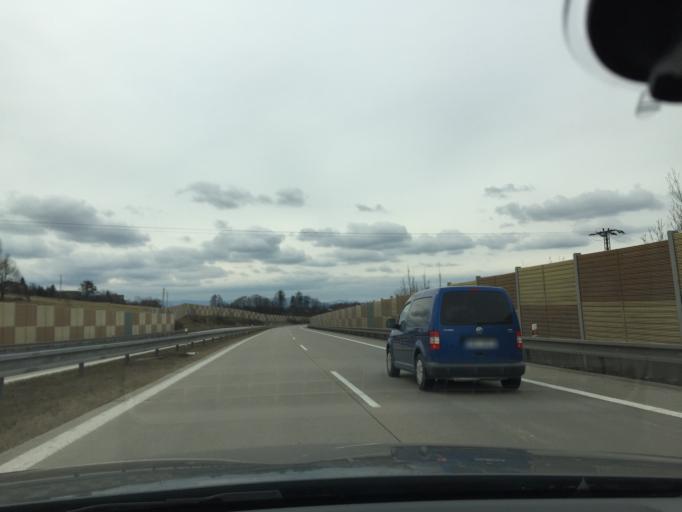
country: CZ
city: Chotebuz
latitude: 49.7173
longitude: 18.5609
